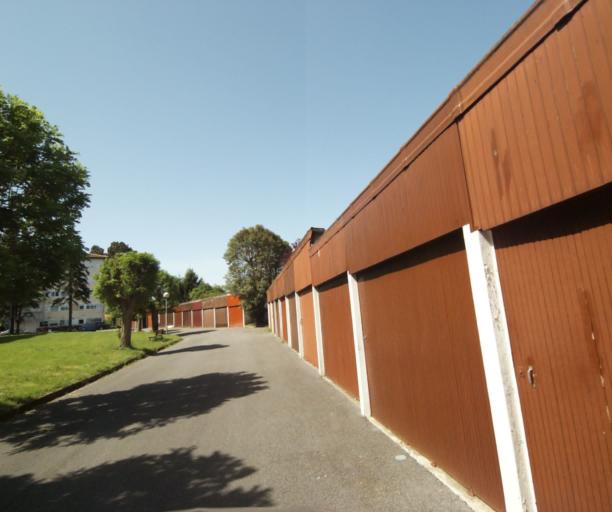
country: FR
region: Aquitaine
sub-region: Departement des Pyrenees-Atlantiques
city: Bayonne
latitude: 43.4784
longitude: -1.4607
